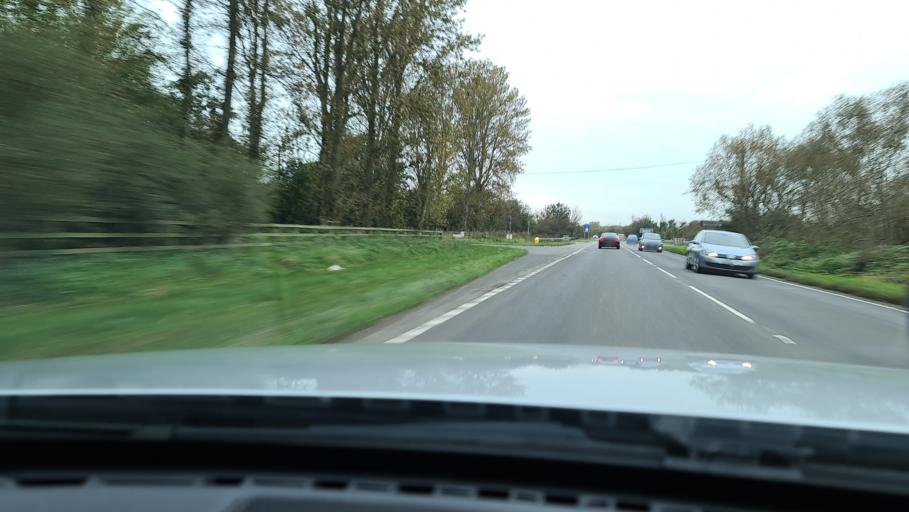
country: GB
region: England
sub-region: Oxfordshire
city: Bicester
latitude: 51.8753
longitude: -1.0788
